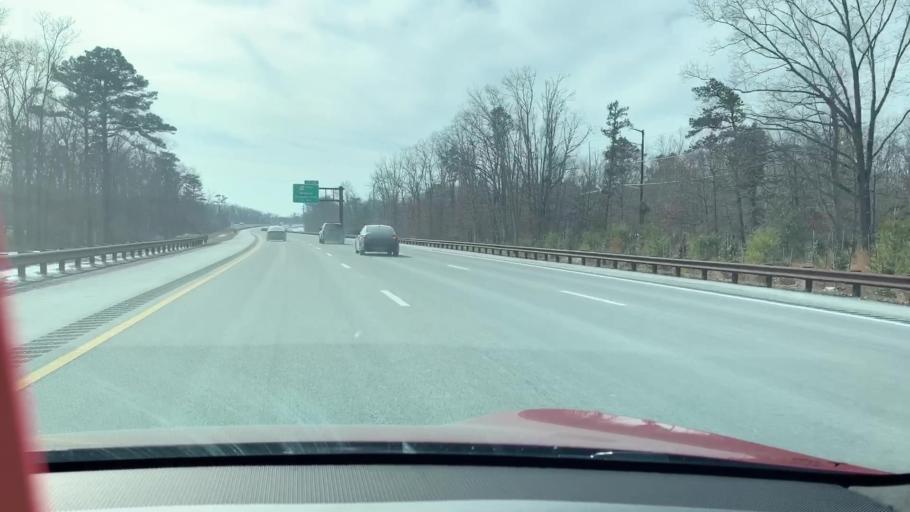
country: US
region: New Jersey
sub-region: Atlantic County
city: Pomona
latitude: 39.4595
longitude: -74.5344
